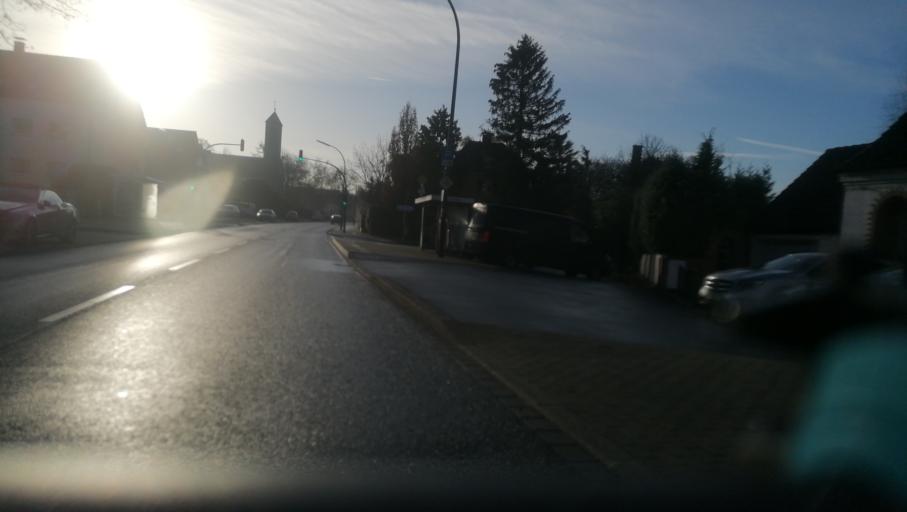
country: DE
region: North Rhine-Westphalia
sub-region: Regierungsbezirk Arnsberg
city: Dortmund
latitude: 51.4678
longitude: 7.4928
